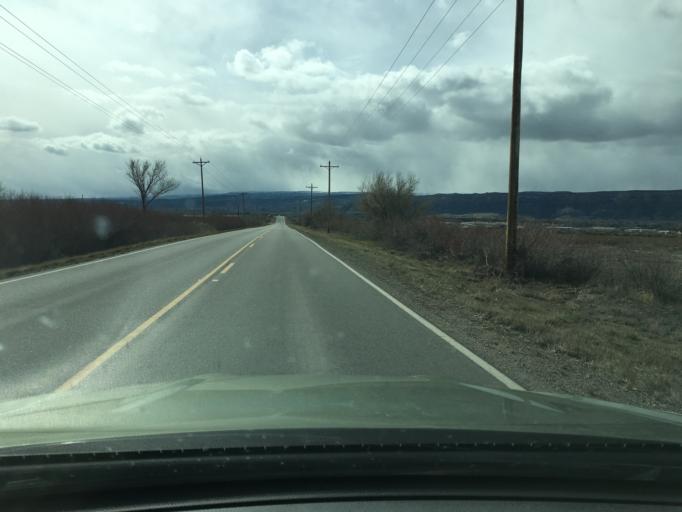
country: US
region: Colorado
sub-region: Mesa County
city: Redlands
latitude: 39.1198
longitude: -108.6267
